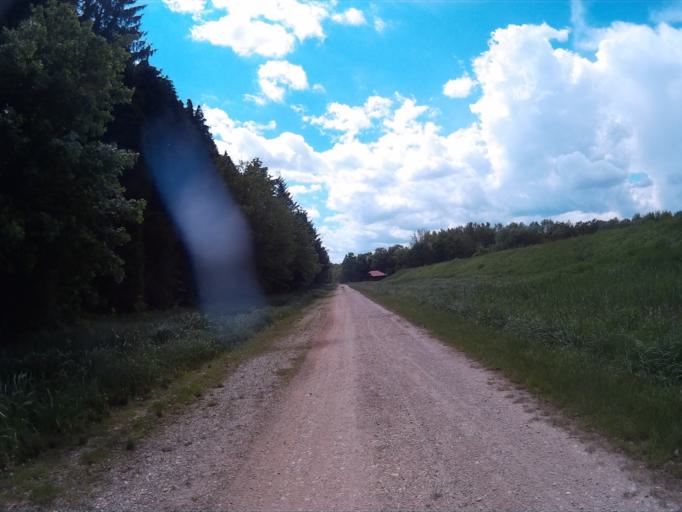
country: HU
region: Vas
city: Kormend
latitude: 46.9589
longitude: 16.5375
